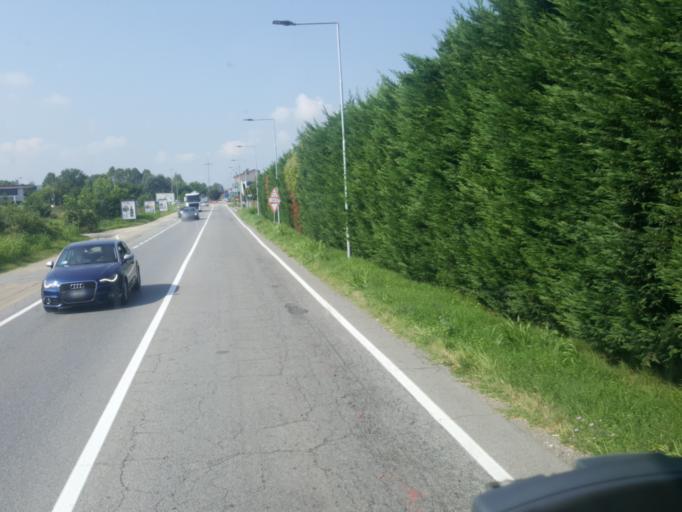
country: IT
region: Piedmont
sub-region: Provincia di Cuneo
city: Mussotto
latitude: 44.7134
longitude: 8.0303
